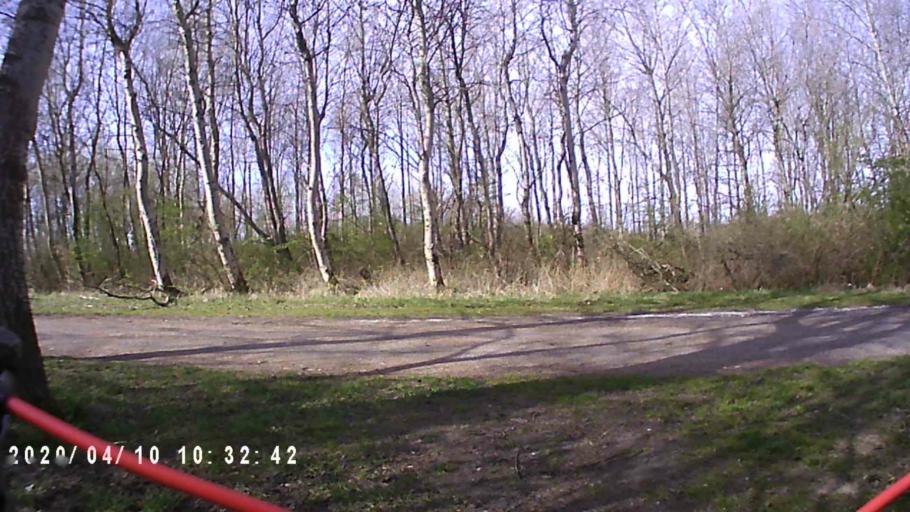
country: NL
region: Friesland
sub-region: Gemeente Dongeradeel
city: Anjum
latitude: 53.3929
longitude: 6.2127
